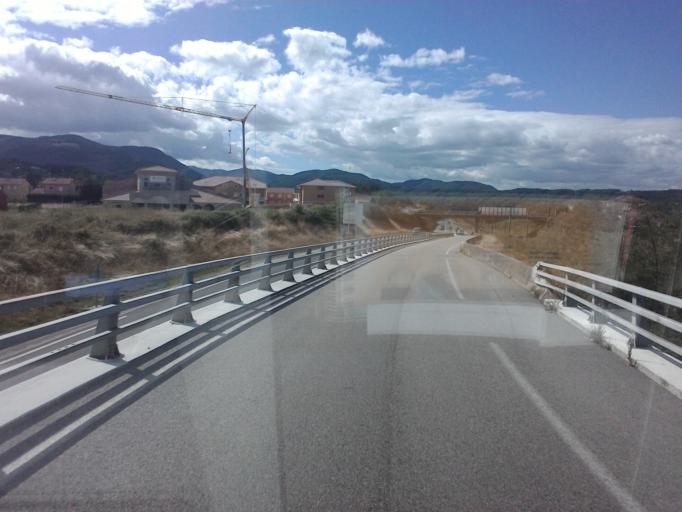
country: FR
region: Rhone-Alpes
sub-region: Departement de l'Ain
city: Amberieu-en-Bugey
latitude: 45.9733
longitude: 5.3465
